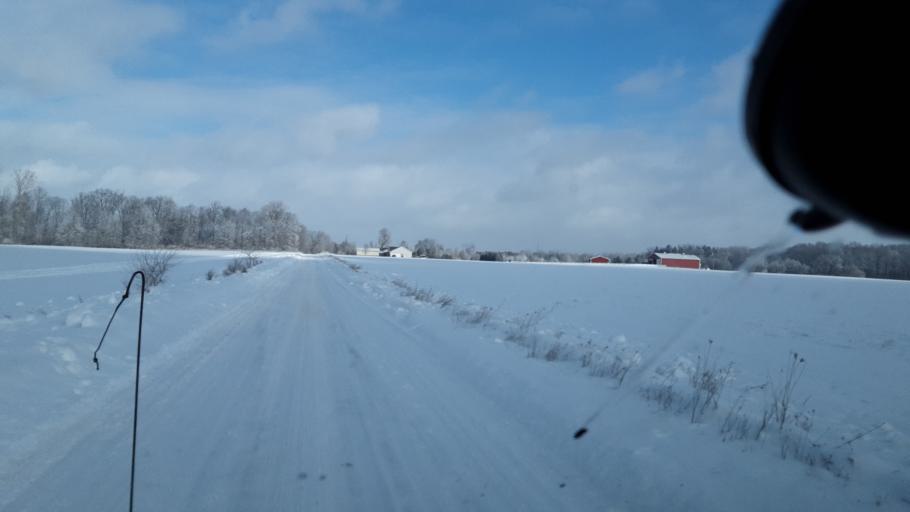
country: US
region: Michigan
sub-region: Eaton County
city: Eaton Rapids
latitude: 42.5169
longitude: -84.6309
